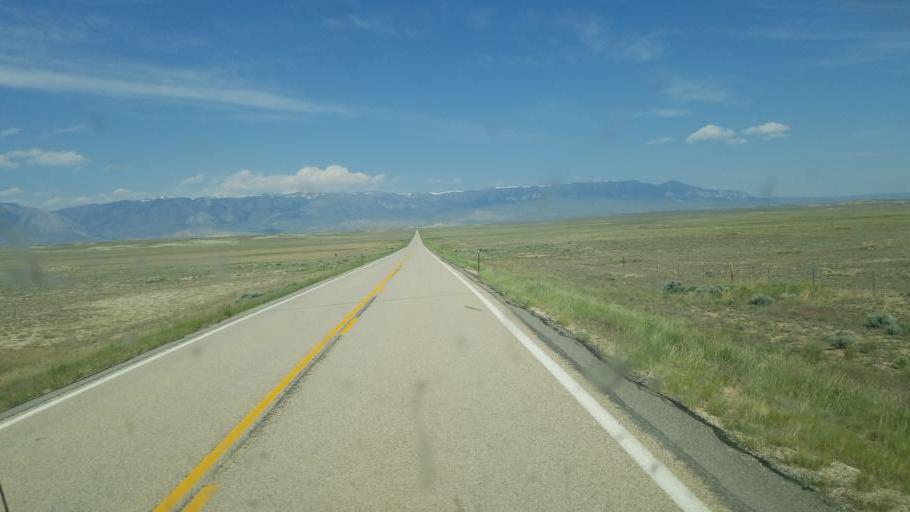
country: US
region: Wyoming
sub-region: Park County
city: Powell
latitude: 44.8577
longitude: -109.0208
